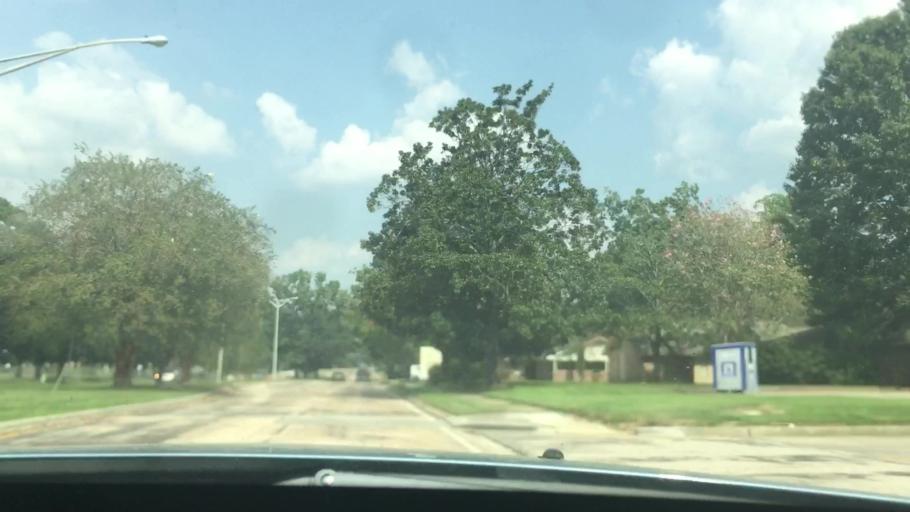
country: US
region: Louisiana
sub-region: East Baton Rouge Parish
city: Westminster
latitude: 30.4422
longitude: -91.1077
